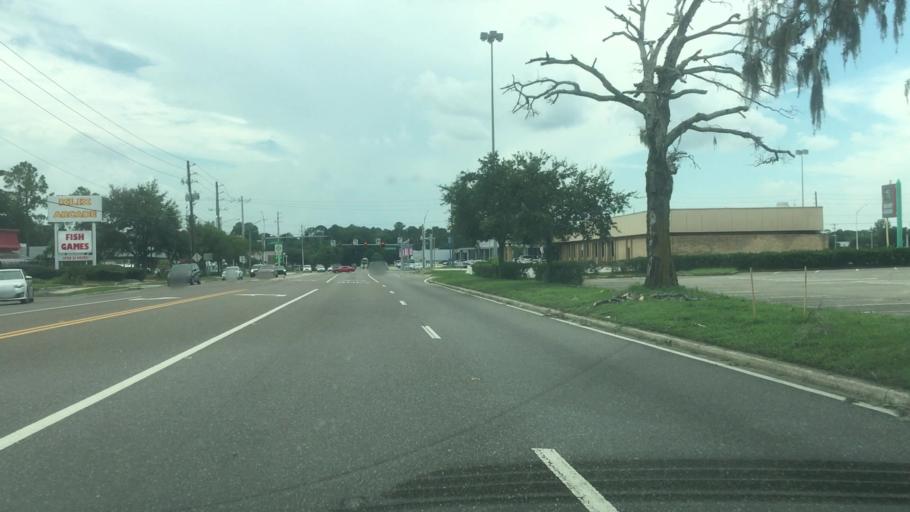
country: US
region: Florida
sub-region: Duval County
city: Jacksonville
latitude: 30.3237
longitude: -81.5469
